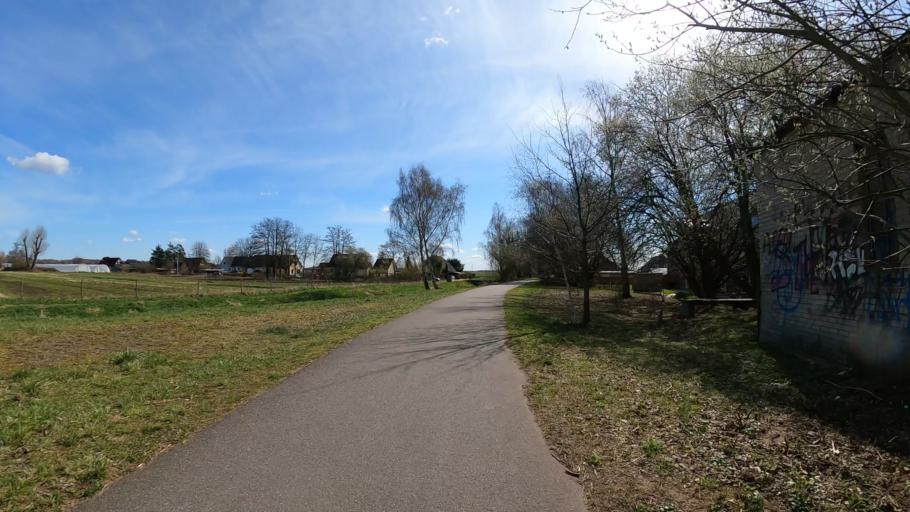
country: DE
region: Hamburg
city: Rothenburgsort
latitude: 53.4732
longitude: 10.0848
